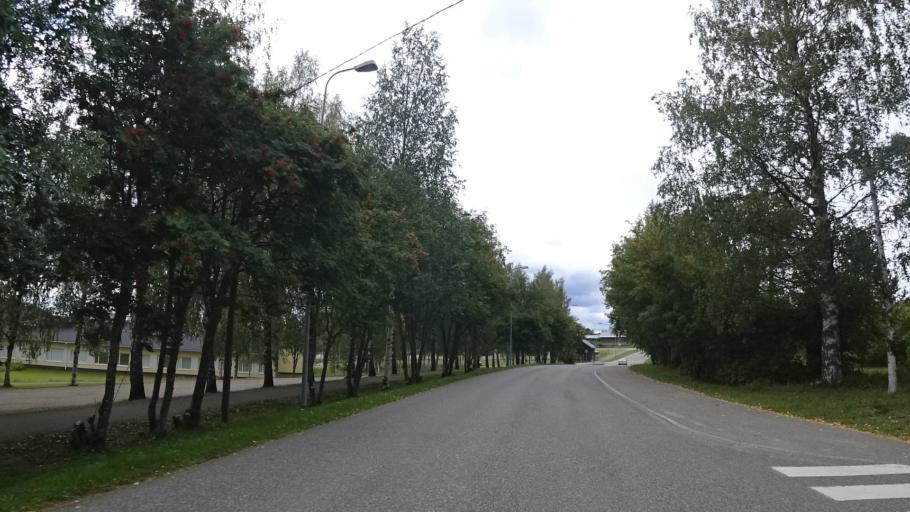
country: FI
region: North Karelia
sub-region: Joensuu
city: Ilomantsi
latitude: 62.6663
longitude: 30.9322
